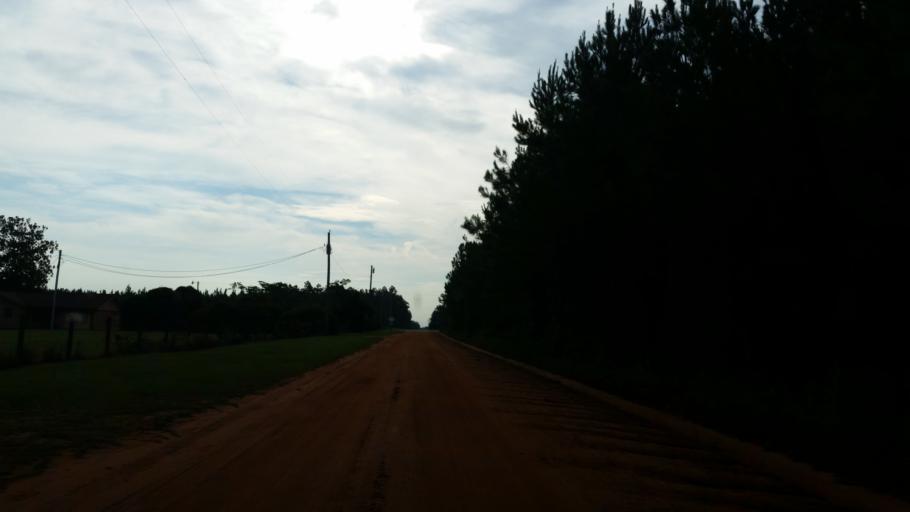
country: US
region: Florida
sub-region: Escambia County
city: Molino
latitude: 30.7928
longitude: -87.5263
